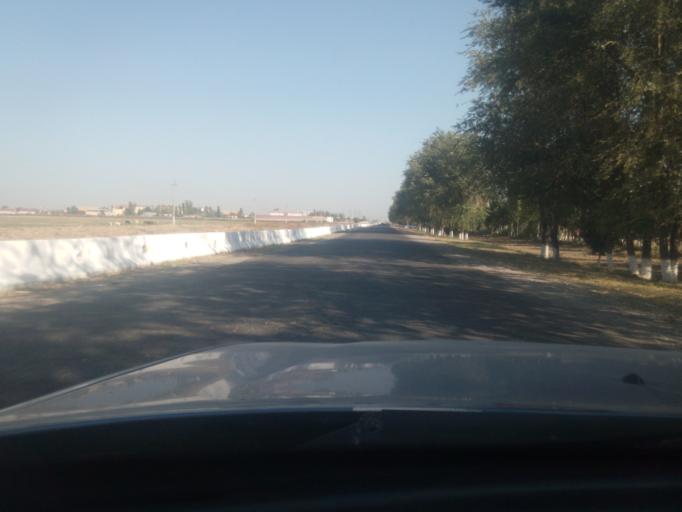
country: UZ
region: Sirdaryo
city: Guliston
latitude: 40.5098
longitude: 68.7956
